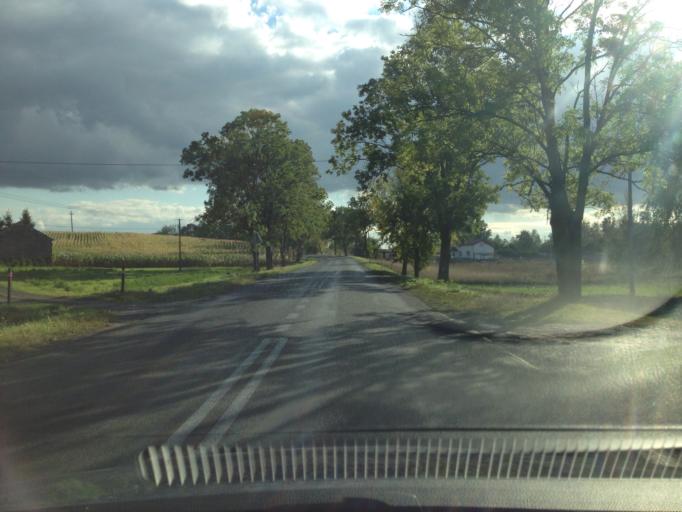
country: PL
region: Kujawsko-Pomorskie
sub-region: Powiat rypinski
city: Rypin
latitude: 53.0567
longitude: 19.3717
